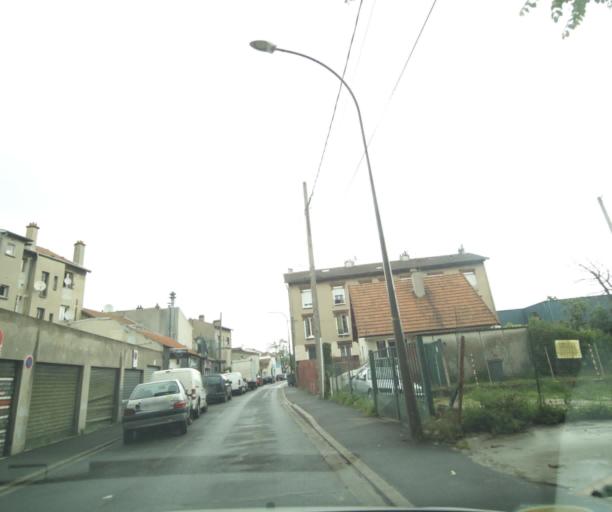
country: FR
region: Ile-de-France
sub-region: Departement du Val-d'Oise
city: Argenteuil
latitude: 48.9369
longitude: 2.2406
